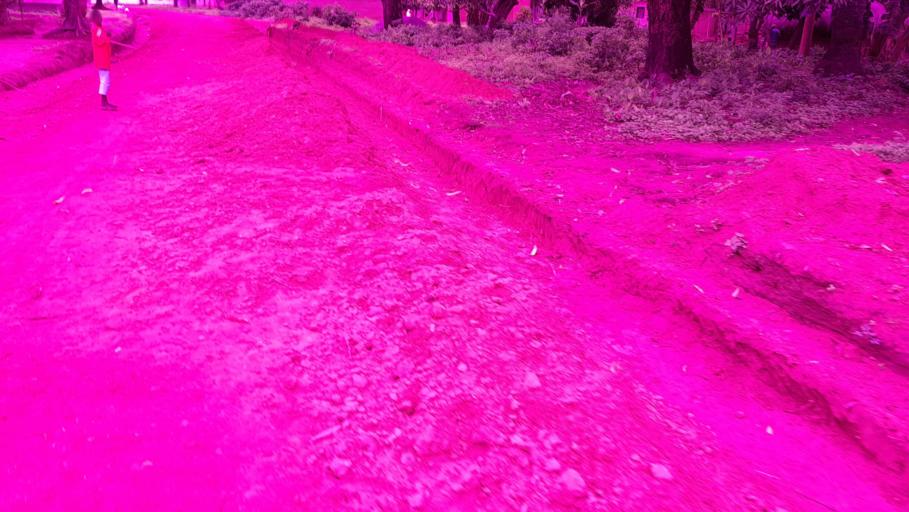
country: GN
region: Boke
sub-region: Boffa
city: Boffa
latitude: 9.9993
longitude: -13.8865
